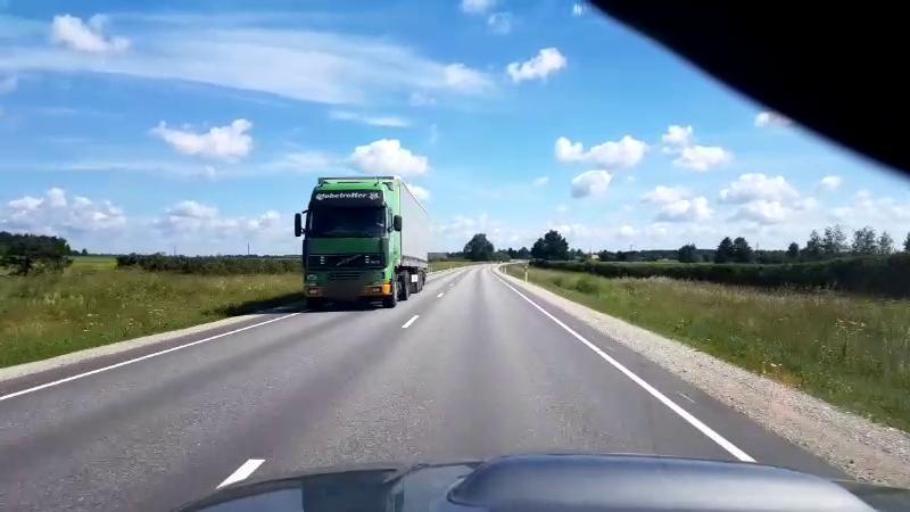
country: EE
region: Jaervamaa
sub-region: Jaerva-Jaani vald
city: Jarva-Jaani
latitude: 59.1036
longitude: 25.7103
